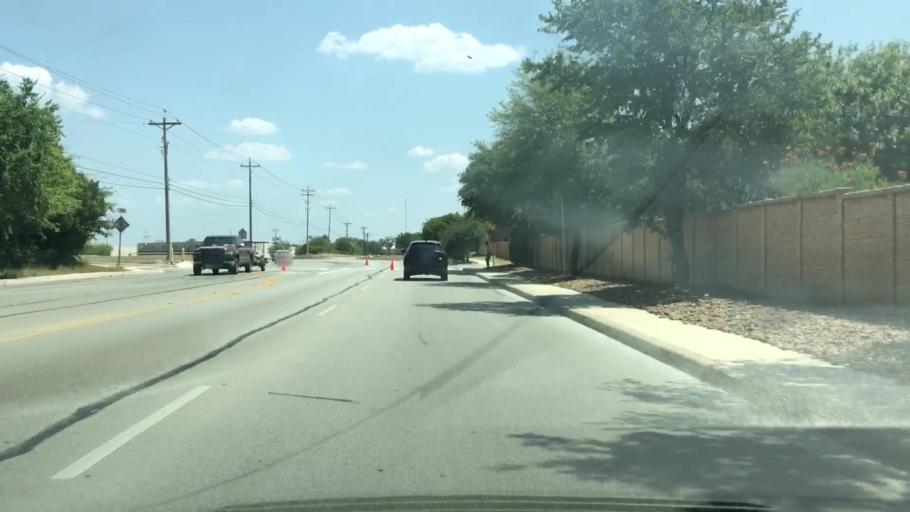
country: US
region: Texas
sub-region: Guadalupe County
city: Northcliff
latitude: 29.5959
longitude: -98.2555
